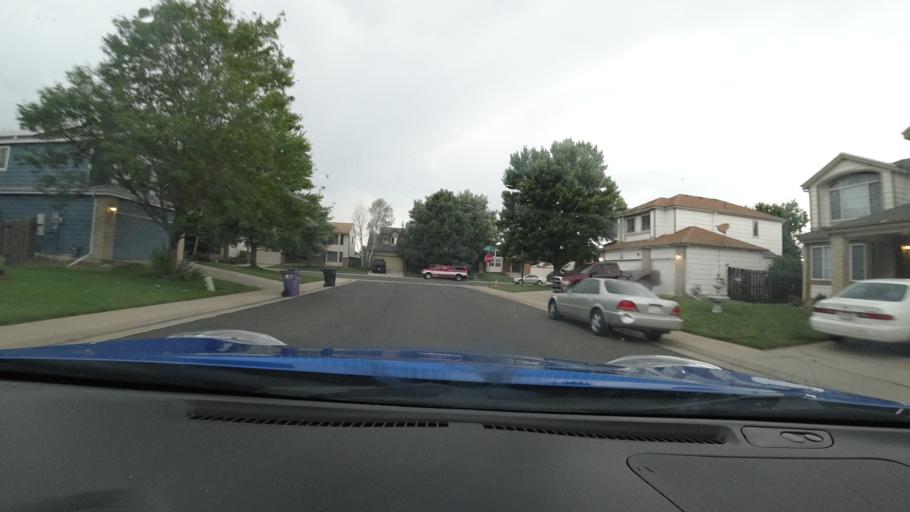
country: US
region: Colorado
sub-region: Adams County
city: Aurora
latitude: 39.7764
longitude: -104.7504
